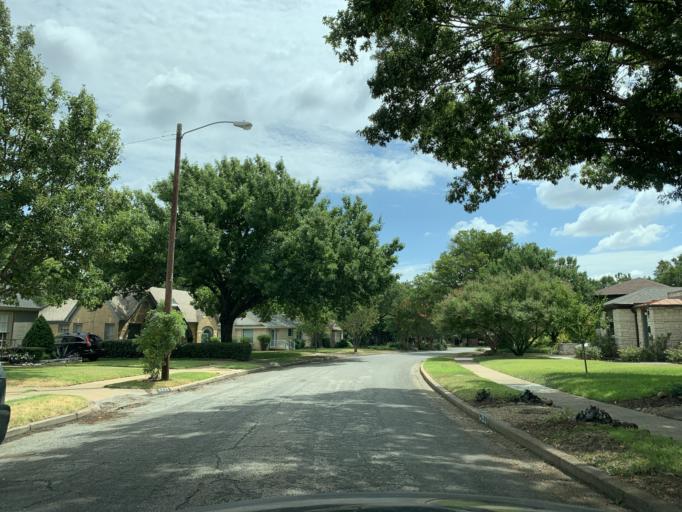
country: US
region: Texas
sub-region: Dallas County
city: Cockrell Hill
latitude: 32.7627
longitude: -96.8597
